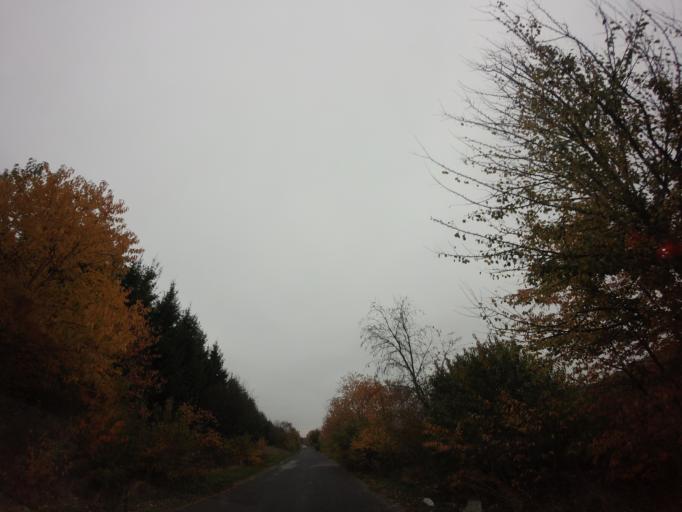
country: PL
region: West Pomeranian Voivodeship
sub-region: Powiat choszczenski
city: Bierzwnik
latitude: 53.1133
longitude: 15.6419
